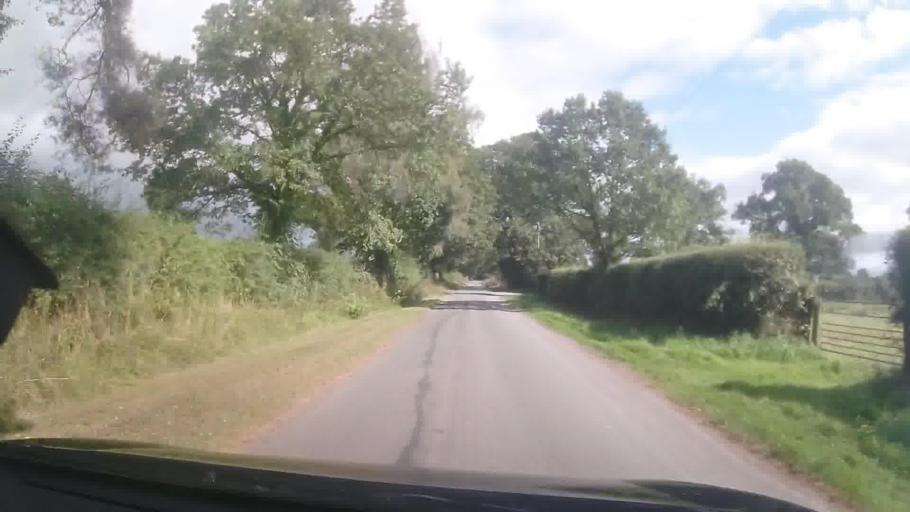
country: GB
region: England
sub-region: Shropshire
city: Prees
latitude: 52.8820
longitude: -2.6322
